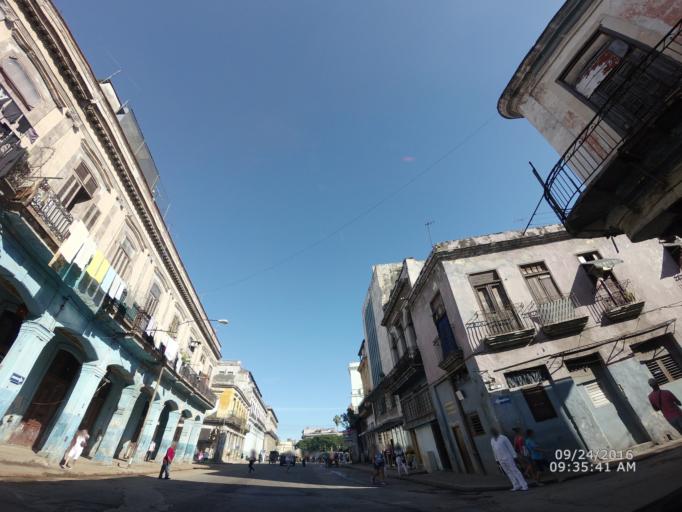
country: CU
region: La Habana
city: La Habana Vieja
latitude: 23.1327
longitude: -82.3558
